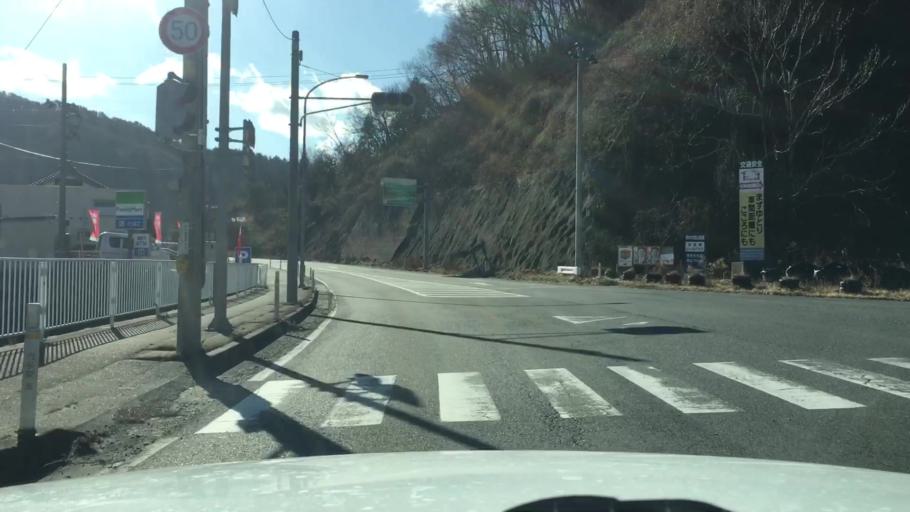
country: JP
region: Iwate
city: Miyako
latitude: 39.6193
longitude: 141.8009
